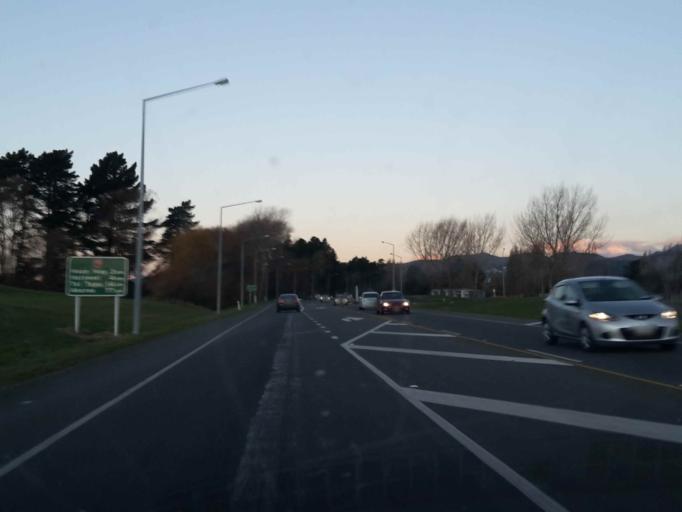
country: NZ
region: Canterbury
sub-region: Christchurch City
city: Christchurch
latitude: -43.5496
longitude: 172.5839
